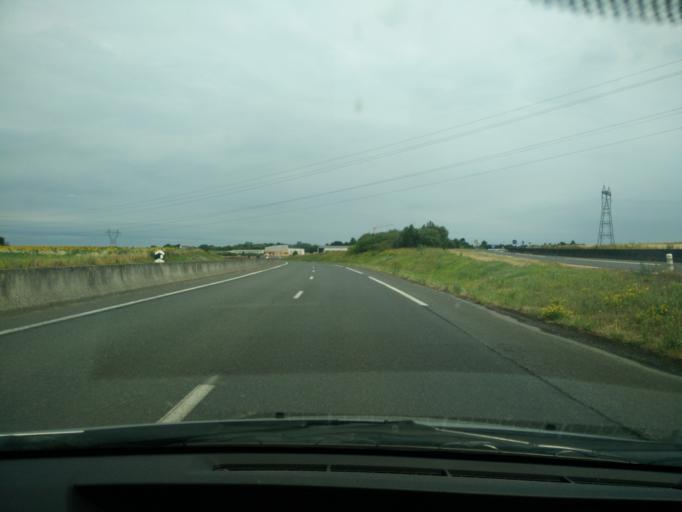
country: FR
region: Pays de la Loire
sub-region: Departement de Maine-et-Loire
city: Doue-la-Fontaine
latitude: 47.2292
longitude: -0.3091
